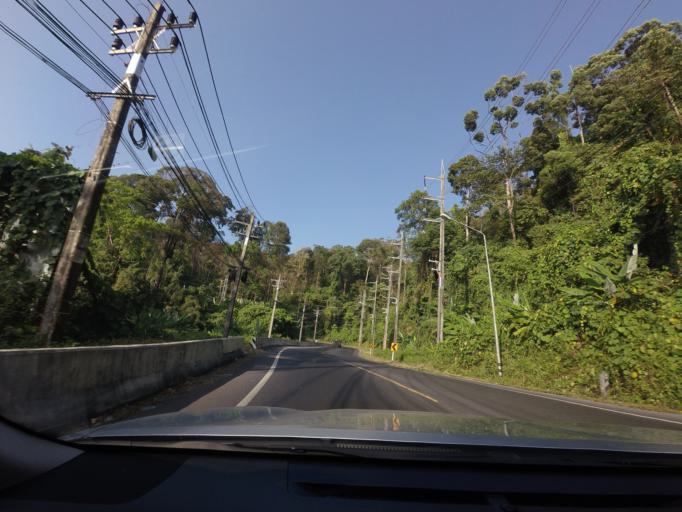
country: TH
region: Phangnga
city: Ban Khao Lak
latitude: 8.6173
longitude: 98.2422
